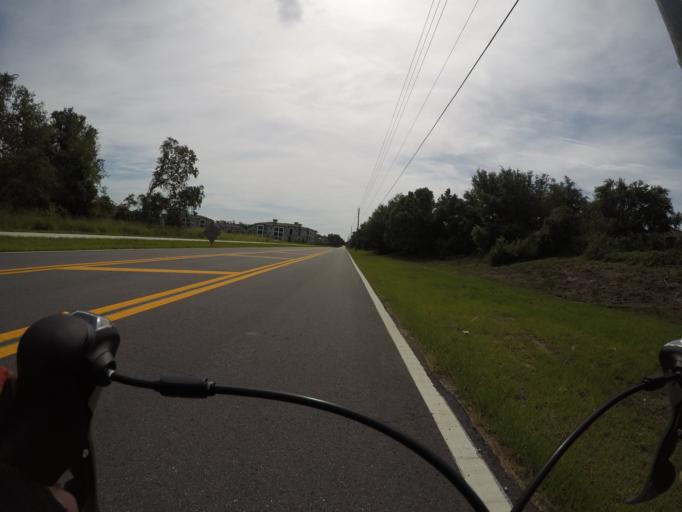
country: US
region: Florida
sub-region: Osceola County
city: Buenaventura Lakes
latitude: 28.3782
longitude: -81.2432
